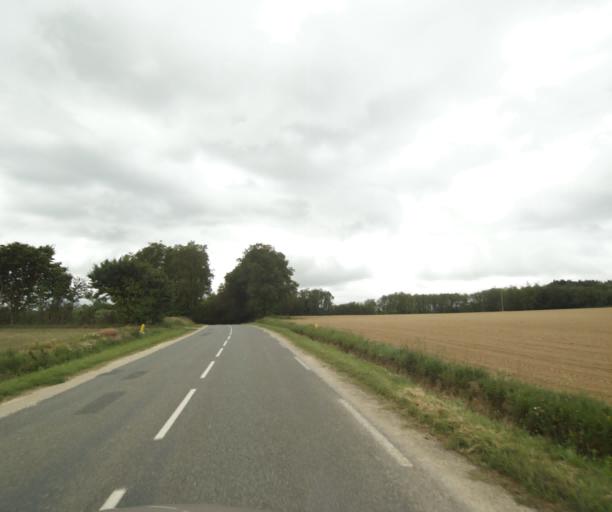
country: FR
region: Rhone-Alpes
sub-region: Departement de l'Ain
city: Miribel
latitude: 45.8478
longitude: 4.9587
